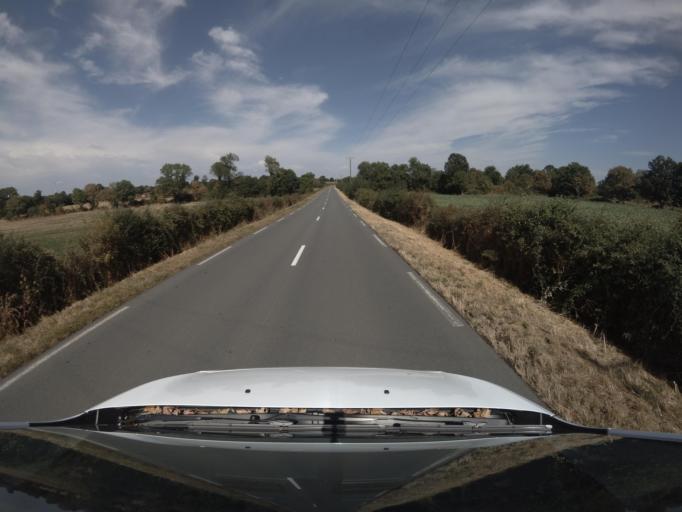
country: FR
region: Poitou-Charentes
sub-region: Departement des Deux-Sevres
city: Nueil-les-Aubiers
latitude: 46.9744
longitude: -0.5434
